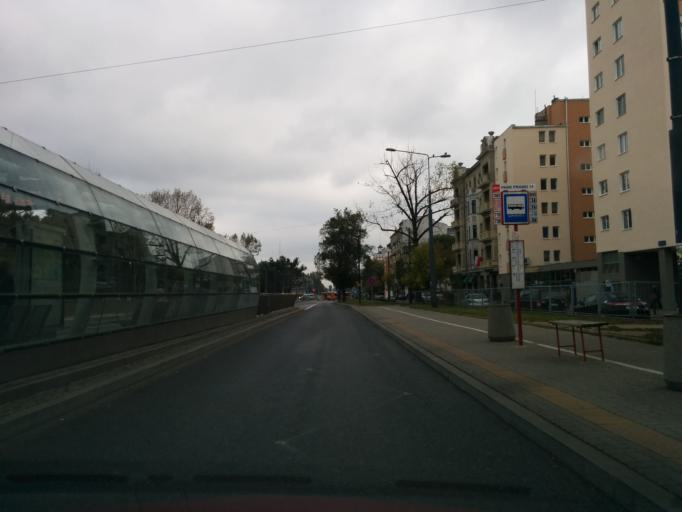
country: PL
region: Masovian Voivodeship
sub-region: Warszawa
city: Praga Polnoc
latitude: 52.2525
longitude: 21.0298
